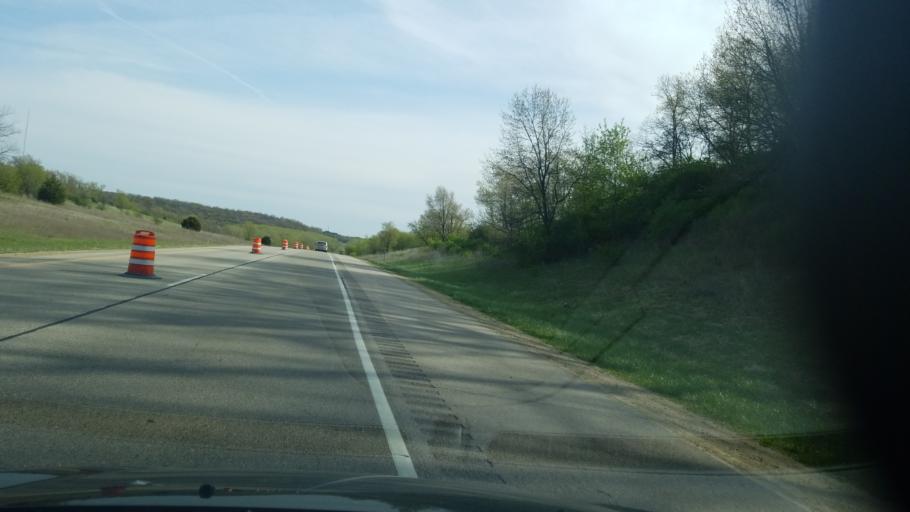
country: US
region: Wisconsin
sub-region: Dane County
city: Oregon
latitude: 42.9762
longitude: -89.3865
